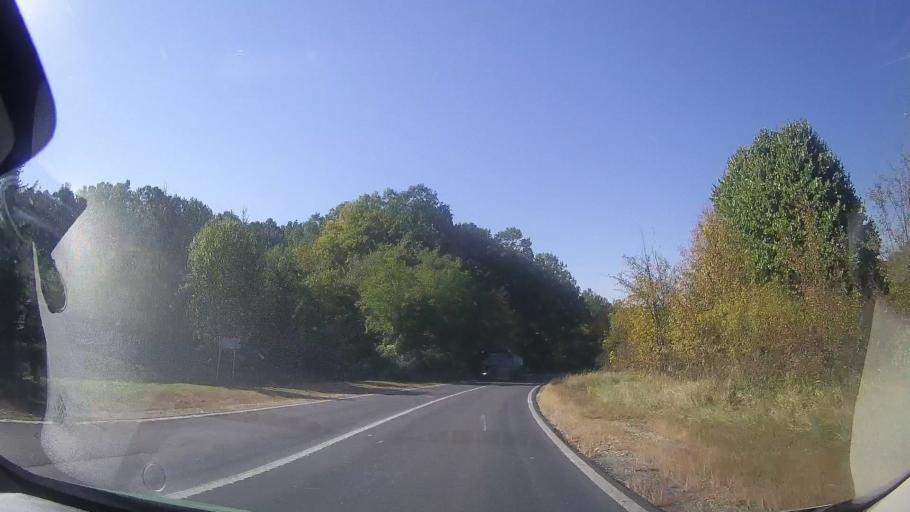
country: RO
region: Timis
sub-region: Comuna Barna
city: Barna
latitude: 45.7177
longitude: 21.9938
